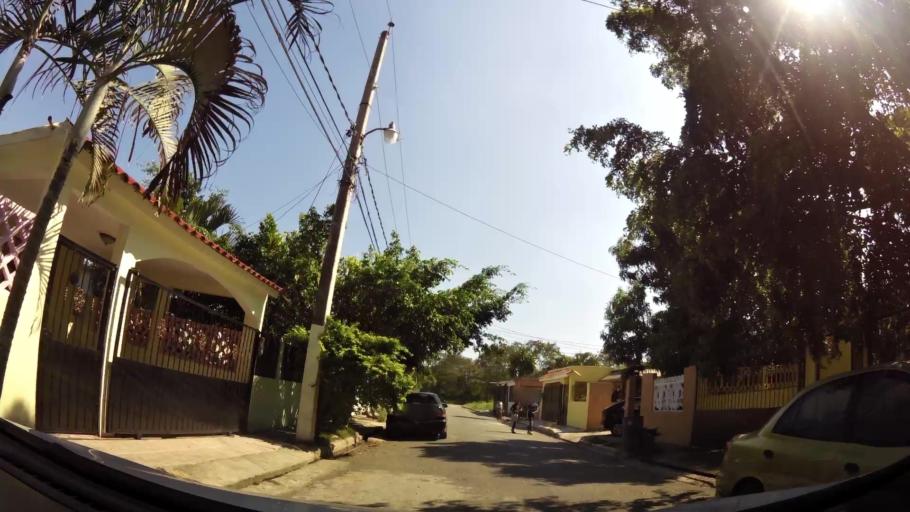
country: DO
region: San Cristobal
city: El Carril
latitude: 18.4711
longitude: -70.0088
